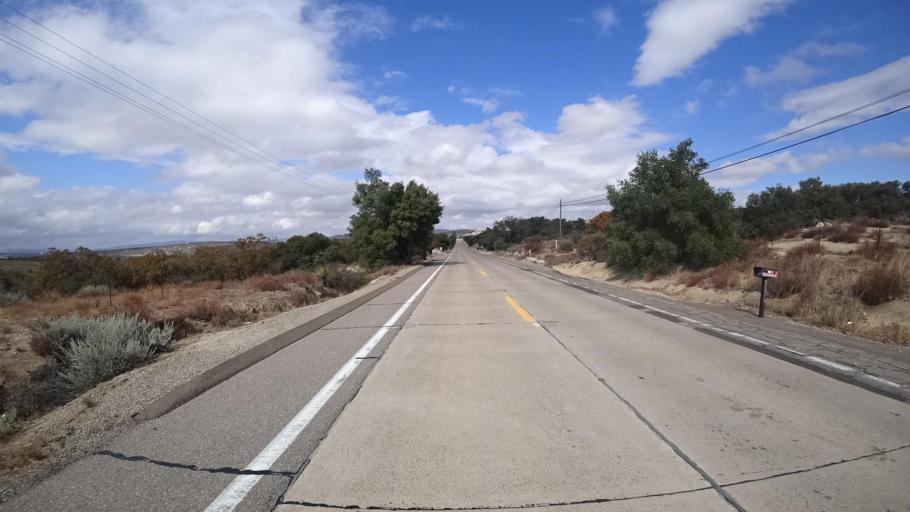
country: US
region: California
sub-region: San Diego County
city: Campo
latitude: 32.6718
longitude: -116.3194
